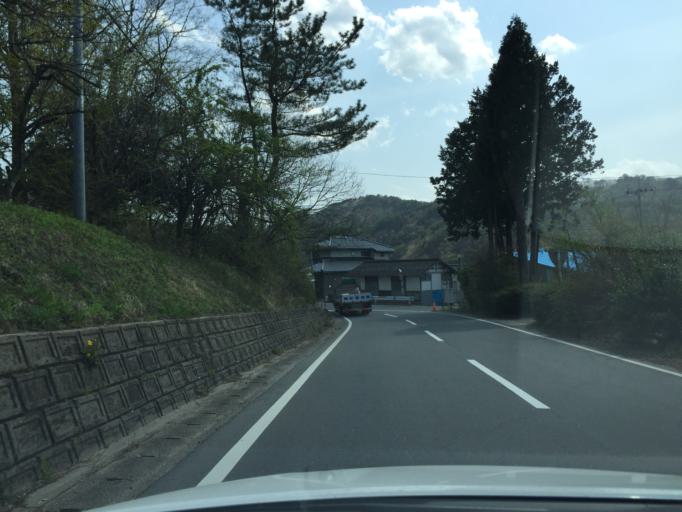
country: JP
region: Fukushima
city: Namie
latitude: 37.3483
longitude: 140.8038
